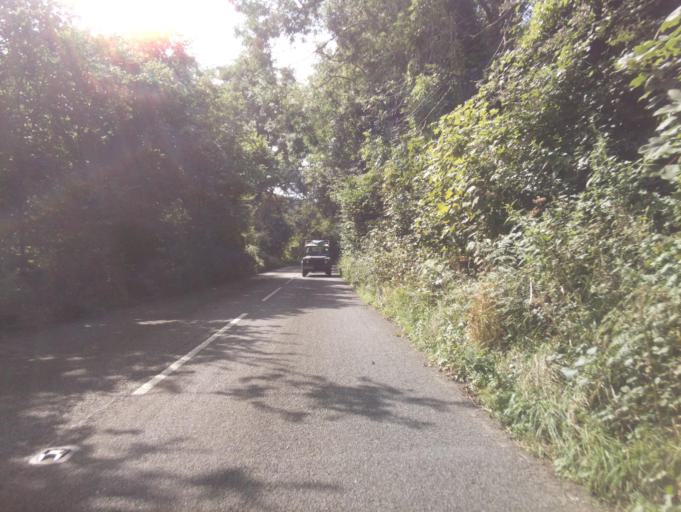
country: GB
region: England
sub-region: Devon
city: Dartmouth
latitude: 50.3587
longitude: -3.5613
